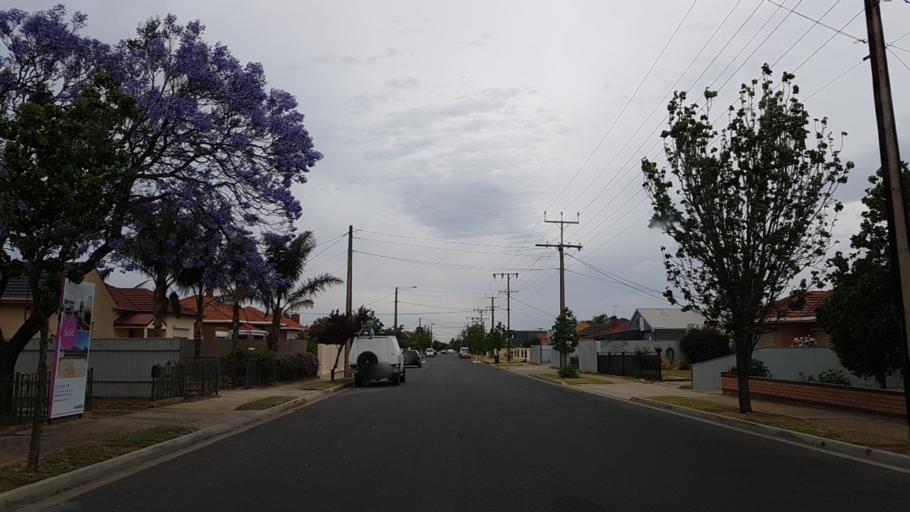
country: AU
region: South Australia
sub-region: Charles Sturt
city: Findon
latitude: -34.8940
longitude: 138.5413
